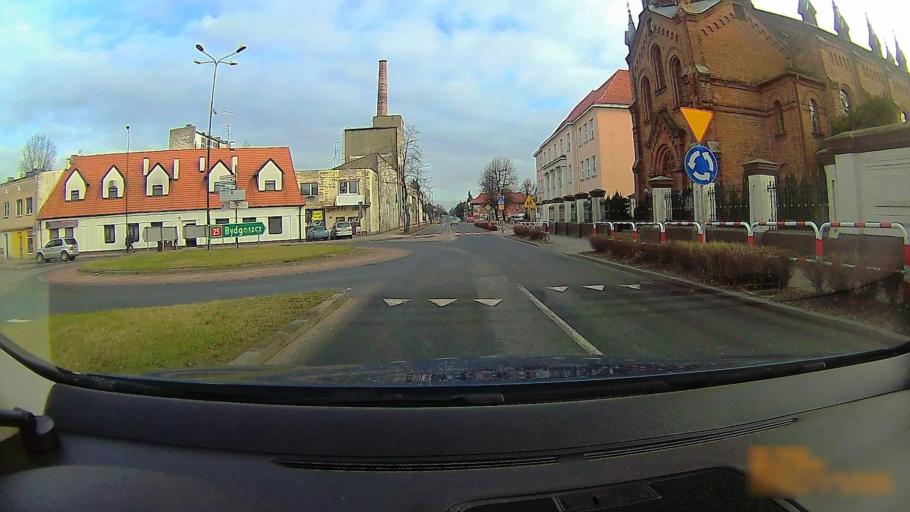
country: PL
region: Greater Poland Voivodeship
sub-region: Konin
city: Konin
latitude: 52.2046
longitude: 18.2534
